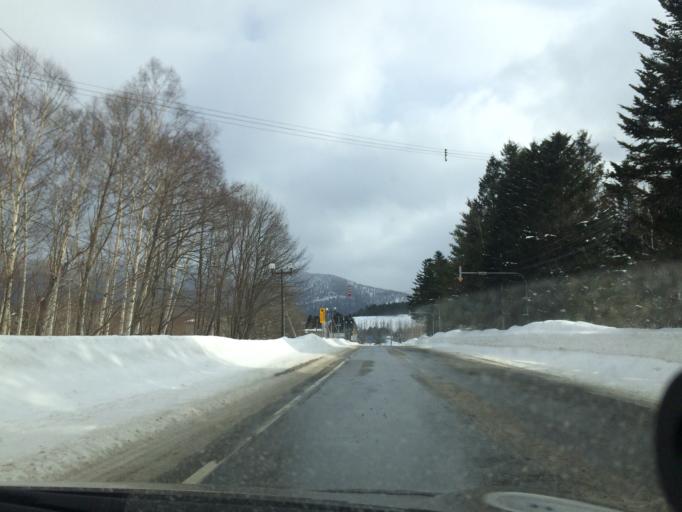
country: JP
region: Hokkaido
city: Shimo-furano
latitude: 43.0457
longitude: 142.6518
